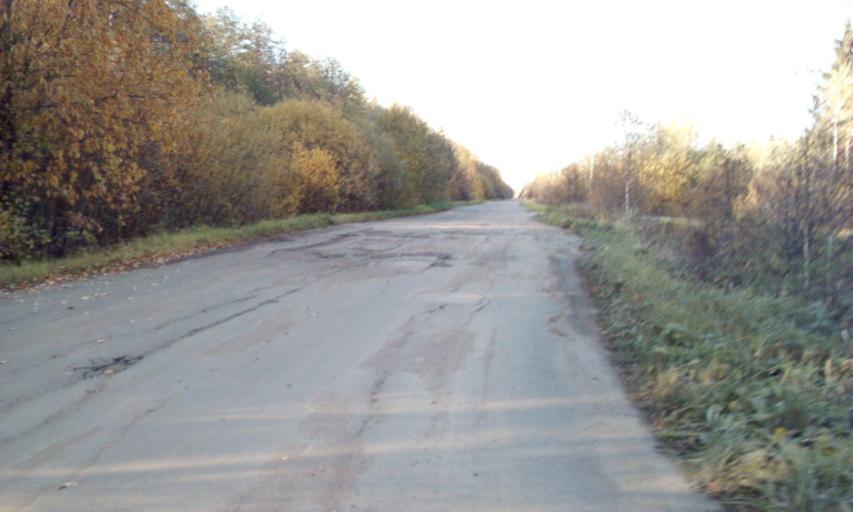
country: RU
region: Moskovskaya
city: Kievskij
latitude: 55.3802
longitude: 36.9105
